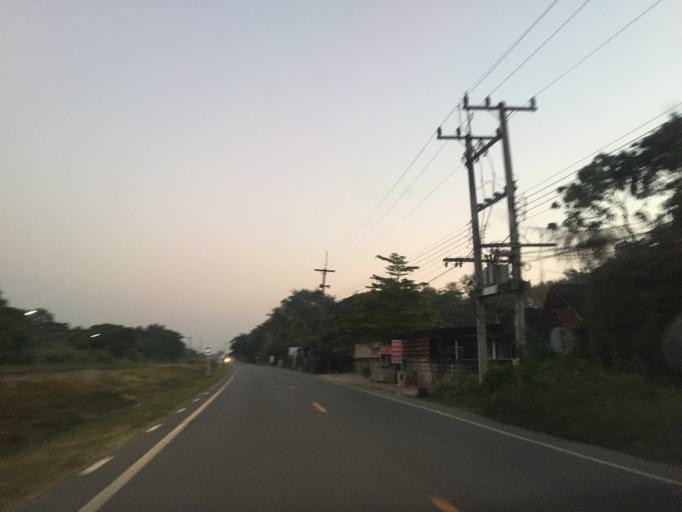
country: TH
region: Chiang Mai
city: Saraphi
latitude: 18.6463
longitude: 99.0446
